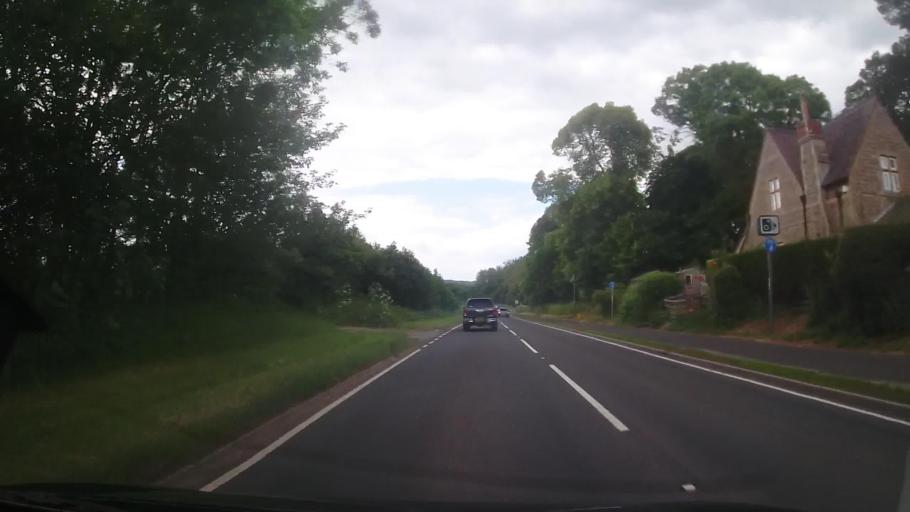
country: GB
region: England
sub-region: Herefordshire
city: Wellington
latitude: 52.1075
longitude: -2.7296
